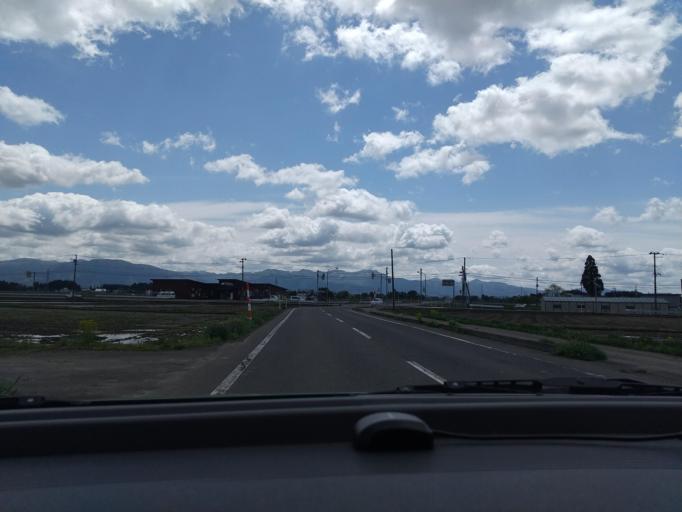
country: JP
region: Akita
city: Kakunodatemachi
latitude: 39.5494
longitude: 140.5568
